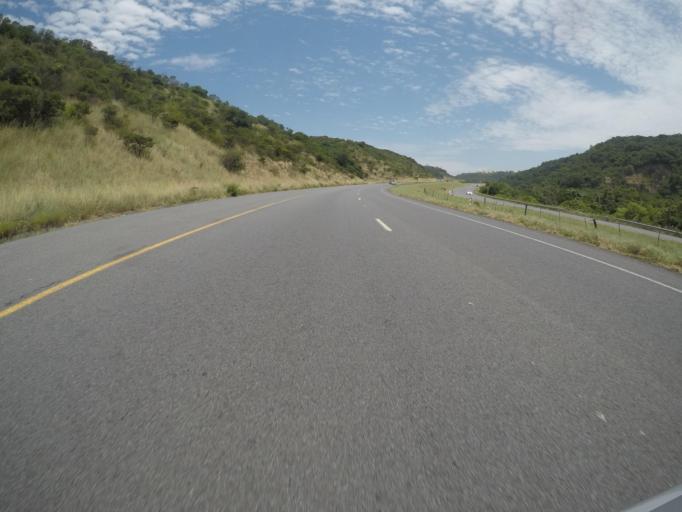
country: ZA
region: Eastern Cape
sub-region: Buffalo City Metropolitan Municipality
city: East London
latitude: -32.9680
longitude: 27.9159
